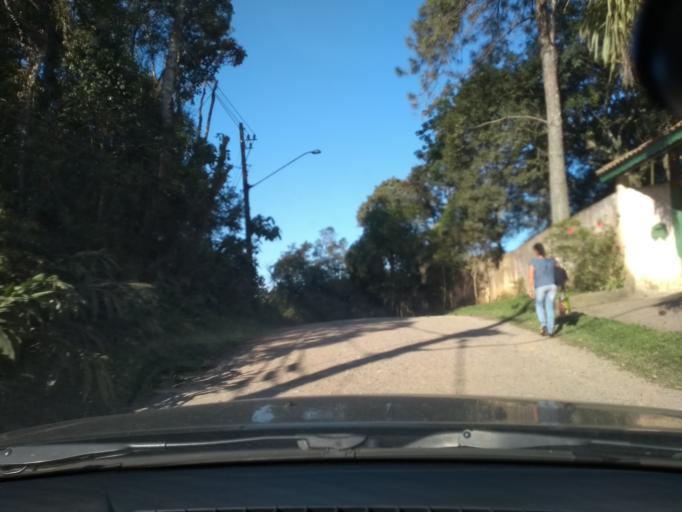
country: BR
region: Sao Paulo
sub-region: Rio Grande Da Serra
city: Rio Grande da Serra
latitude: -23.7629
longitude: -46.4712
